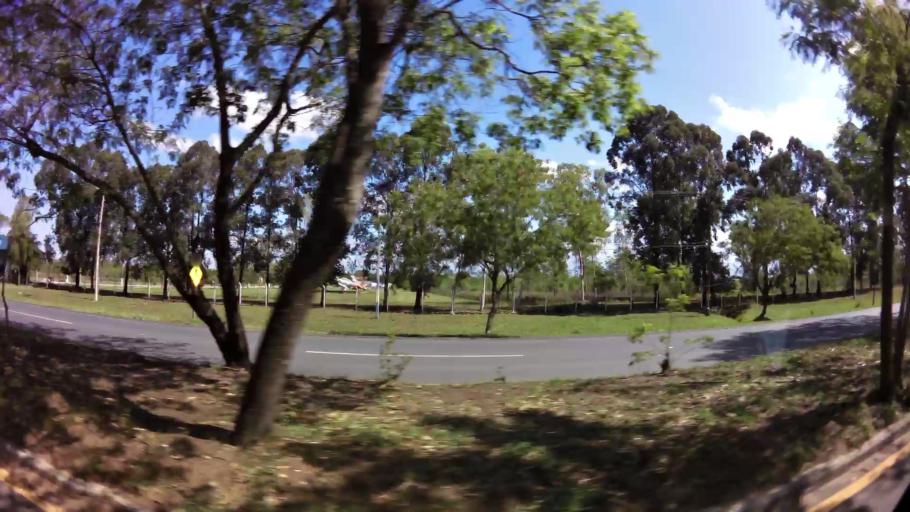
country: PY
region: Central
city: Fernando de la Mora
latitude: -25.2622
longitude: -57.5285
